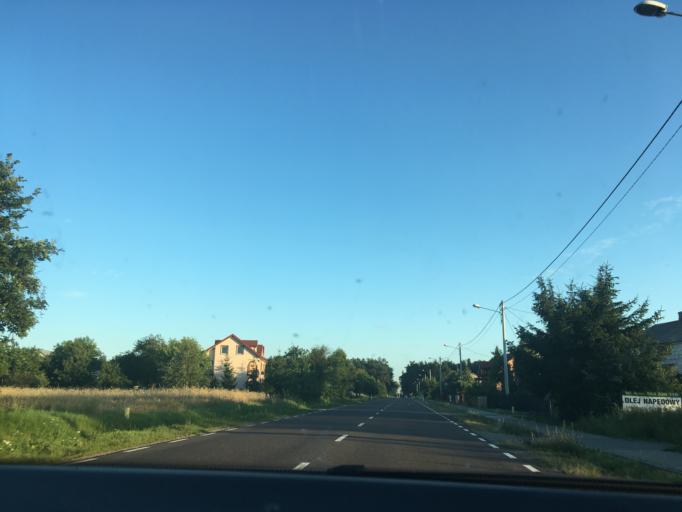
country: PL
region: Lublin Voivodeship
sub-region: Powiat bialski
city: Rzeczyca
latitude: 51.8665
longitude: 22.6980
